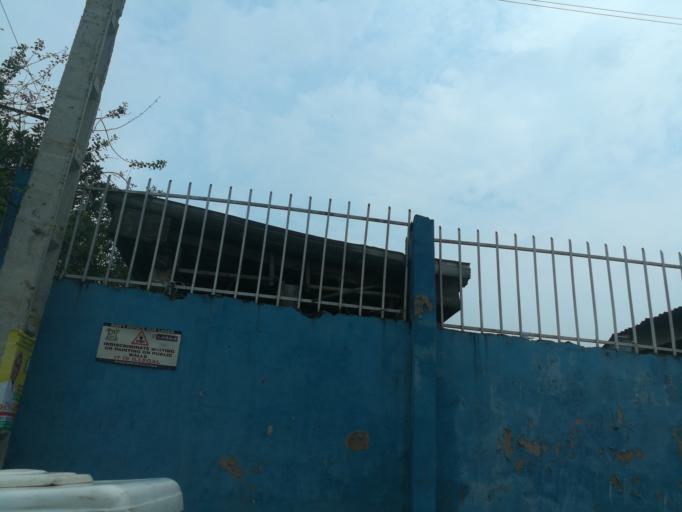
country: NG
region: Lagos
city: Ojota
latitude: 6.6047
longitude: 3.3667
